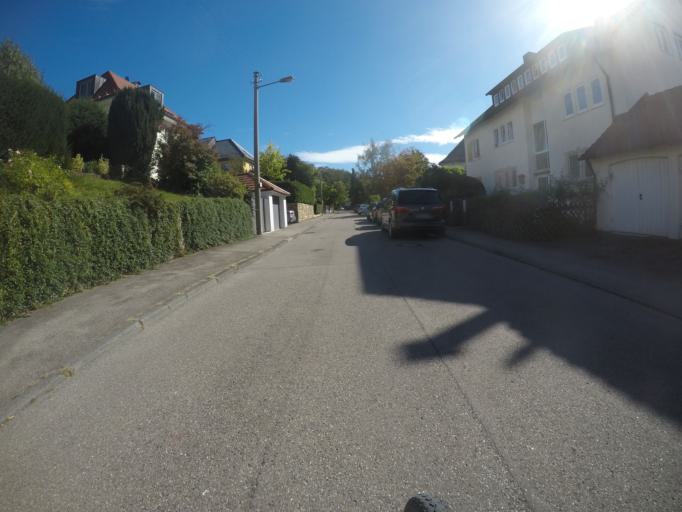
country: DE
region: Baden-Wuerttemberg
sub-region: Regierungsbezirk Stuttgart
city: Stuttgart
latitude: 48.7458
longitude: 9.1783
